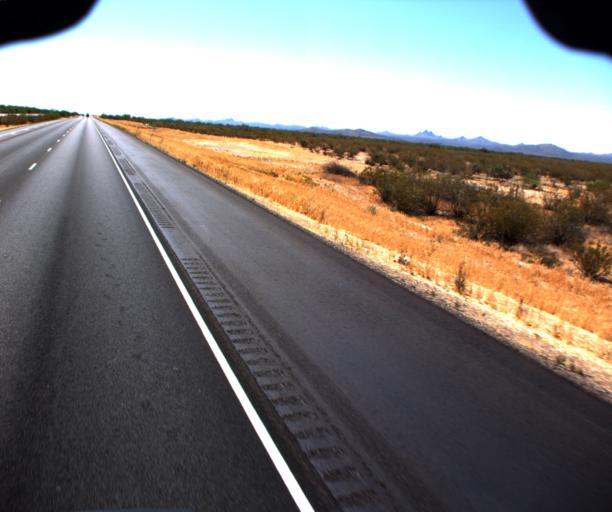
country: US
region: Arizona
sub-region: Yavapai County
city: Congress
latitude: 34.0716
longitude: -112.8767
